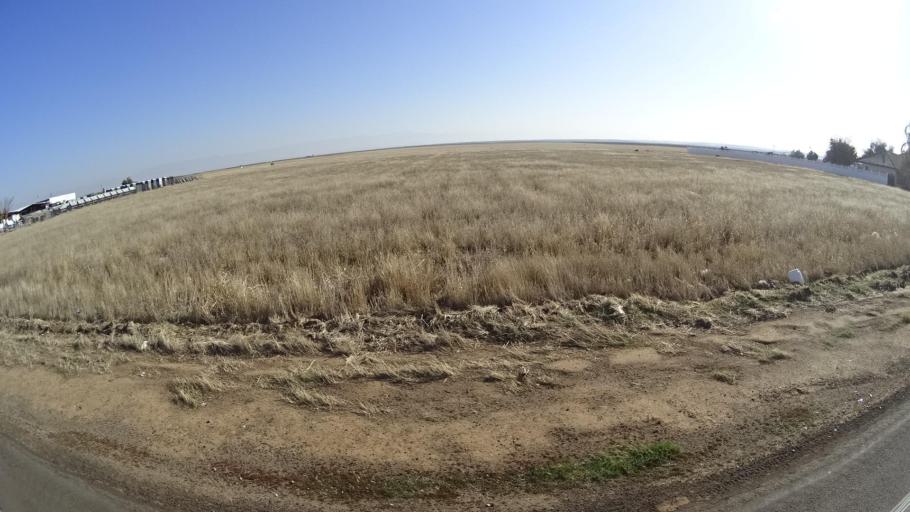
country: US
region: California
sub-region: Tulare County
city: Richgrove
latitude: 35.7492
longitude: -119.1342
